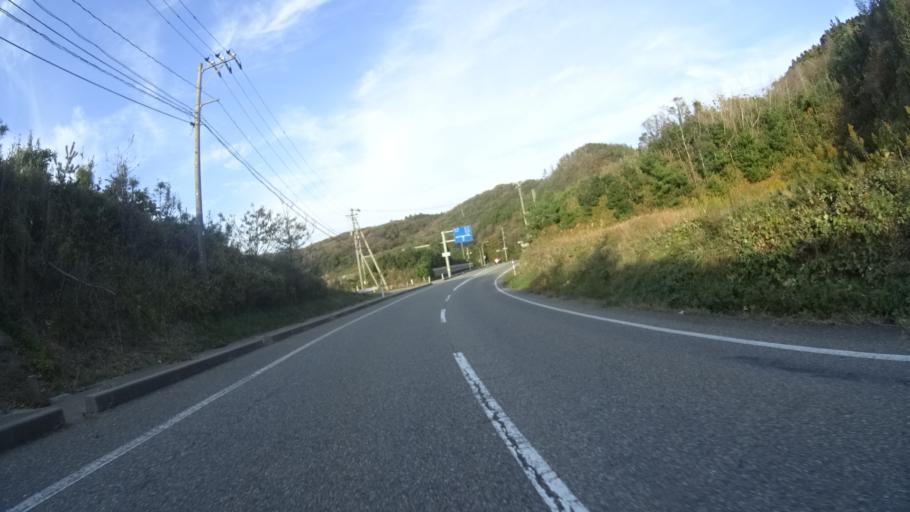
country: JP
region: Ishikawa
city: Hakui
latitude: 37.1021
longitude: 136.7300
